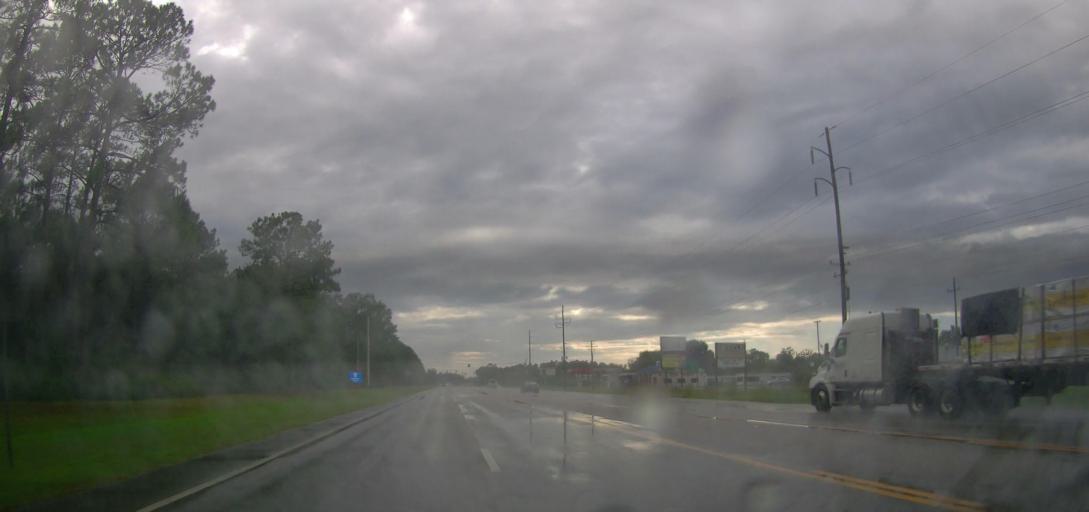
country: US
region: Georgia
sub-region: Ware County
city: Deenwood
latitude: 31.2087
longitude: -82.3858
